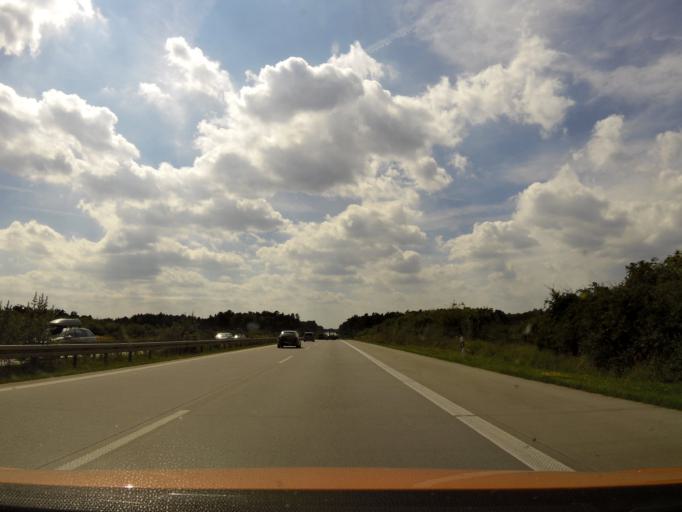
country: DE
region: Brandenburg
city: Marienwerder
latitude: 52.7793
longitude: 13.5731
